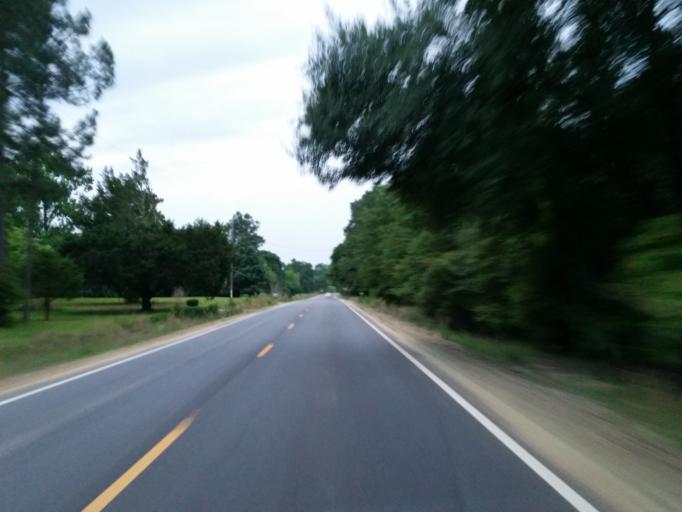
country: US
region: Georgia
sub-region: Turner County
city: Ashburn
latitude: 31.7697
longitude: -83.6886
